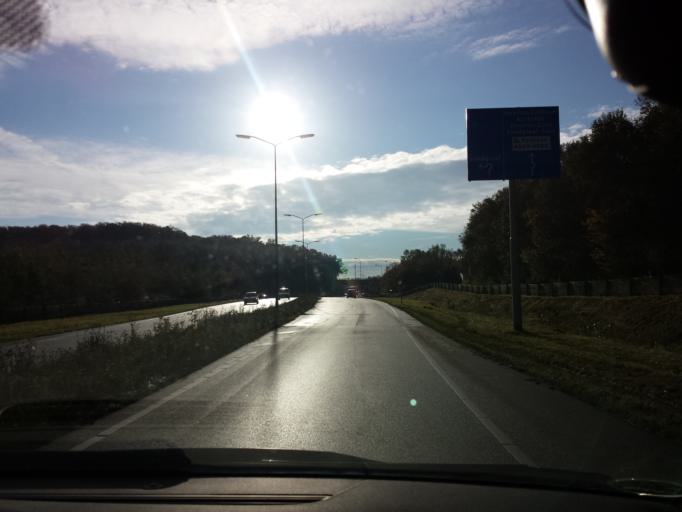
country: NL
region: Limburg
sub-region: Gemeente Heerlen
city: Heerlen
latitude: 50.8944
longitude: 5.9977
